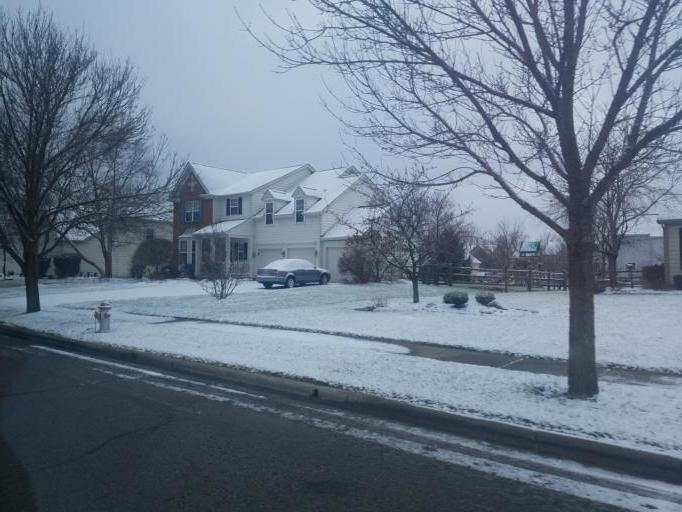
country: US
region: Ohio
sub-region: Franklin County
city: New Albany
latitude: 40.0465
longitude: -82.8168
